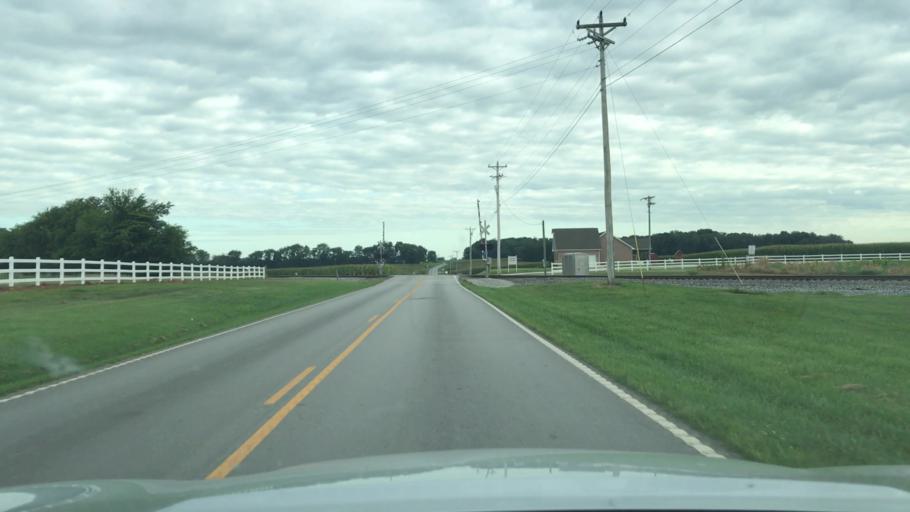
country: US
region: Kentucky
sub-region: Todd County
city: Guthrie
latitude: 36.6770
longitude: -87.1991
